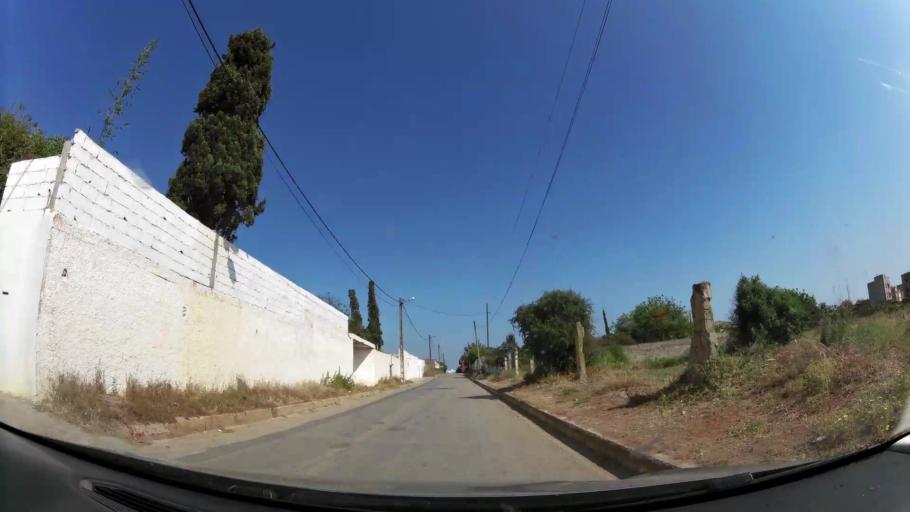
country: MA
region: Rabat-Sale-Zemmour-Zaer
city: Sale
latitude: 34.0738
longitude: -6.7625
